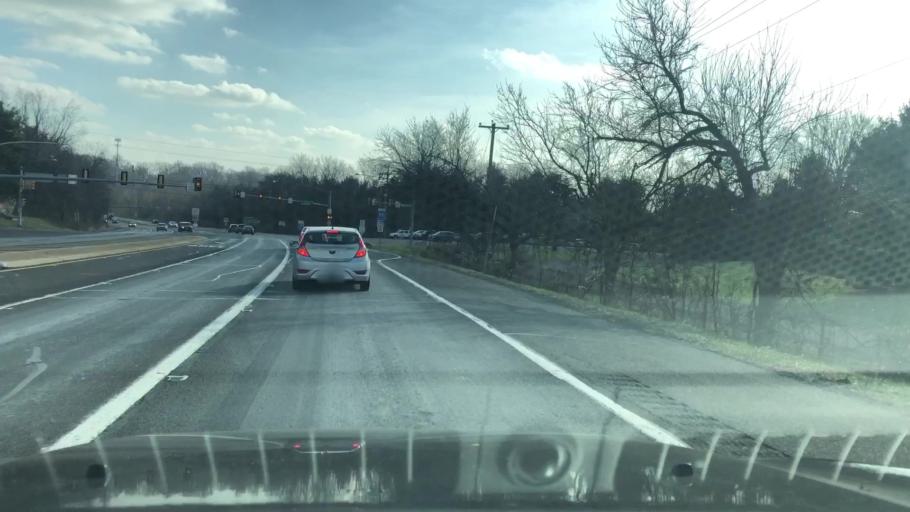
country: US
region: Pennsylvania
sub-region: Bucks County
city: Newtown
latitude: 40.2196
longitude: -74.9443
